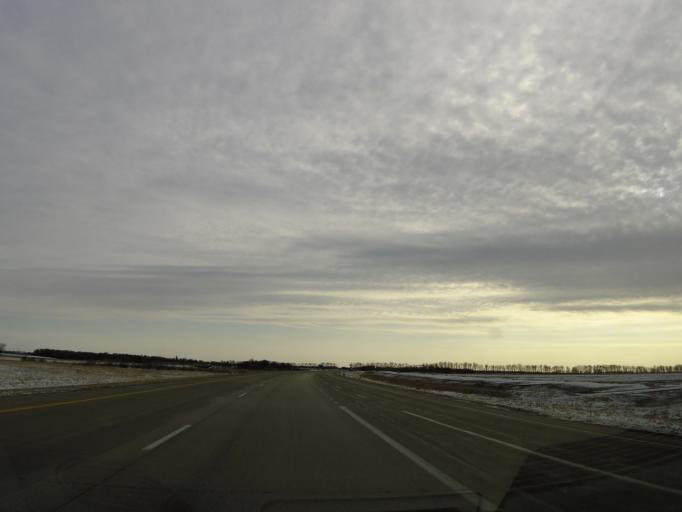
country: US
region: North Dakota
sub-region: Walsh County
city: Grafton
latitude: 48.4672
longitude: -97.1912
